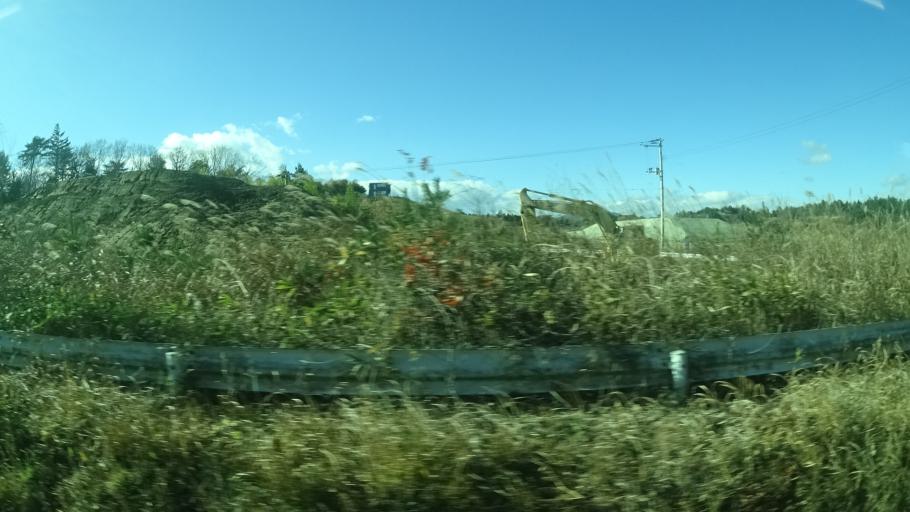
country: JP
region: Fukushima
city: Namie
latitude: 37.6721
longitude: 140.9726
